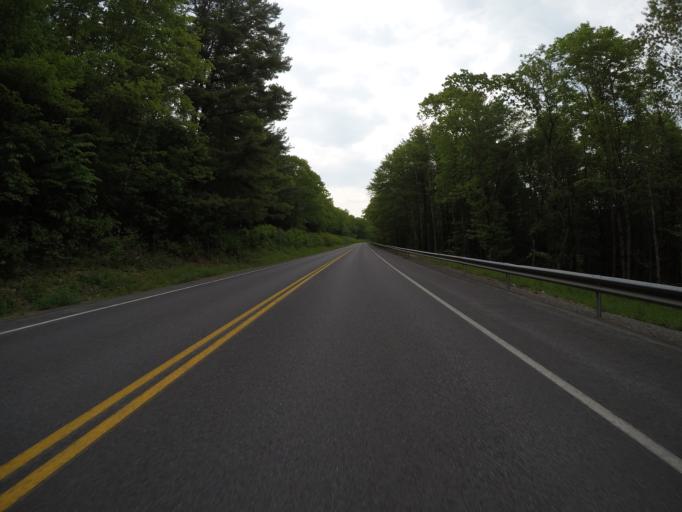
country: US
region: New York
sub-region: Sullivan County
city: Livingston Manor
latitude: 42.0609
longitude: -74.9251
